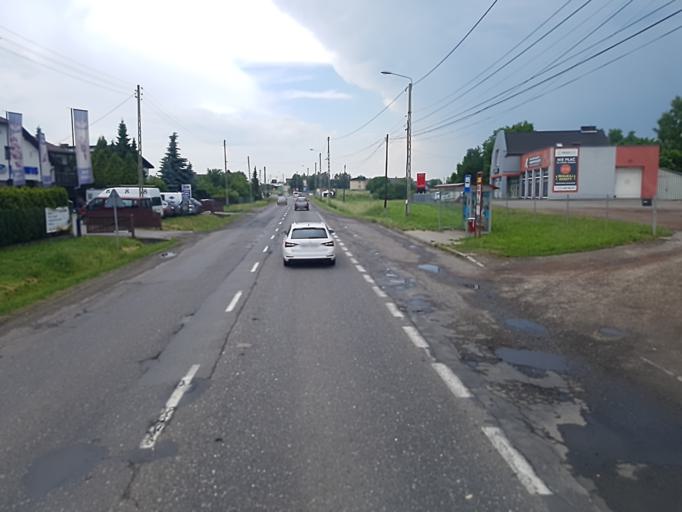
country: PL
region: Silesian Voivodeship
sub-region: Powiat wodzislawski
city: Mszana
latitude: 49.9820
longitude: 18.5135
